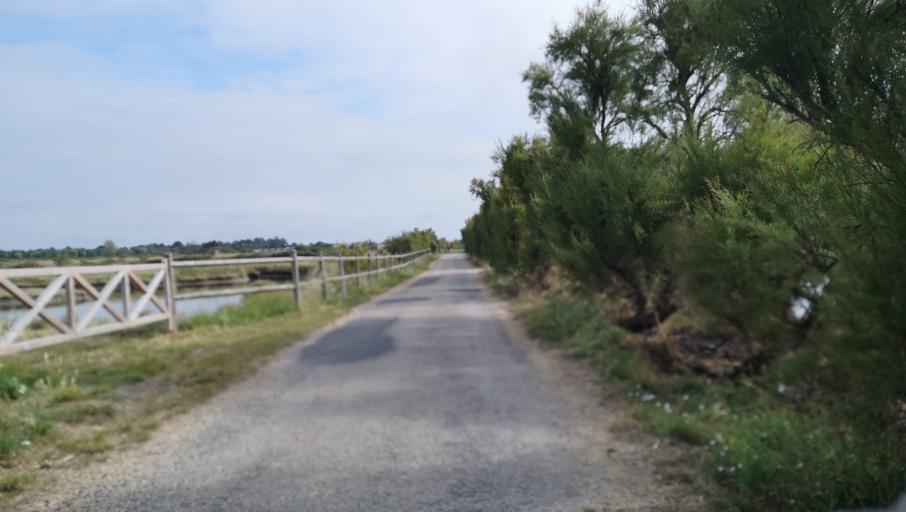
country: FR
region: Pays de la Loire
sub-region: Departement de la Vendee
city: Olonne-sur-Mer
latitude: 46.5370
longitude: -1.8045
